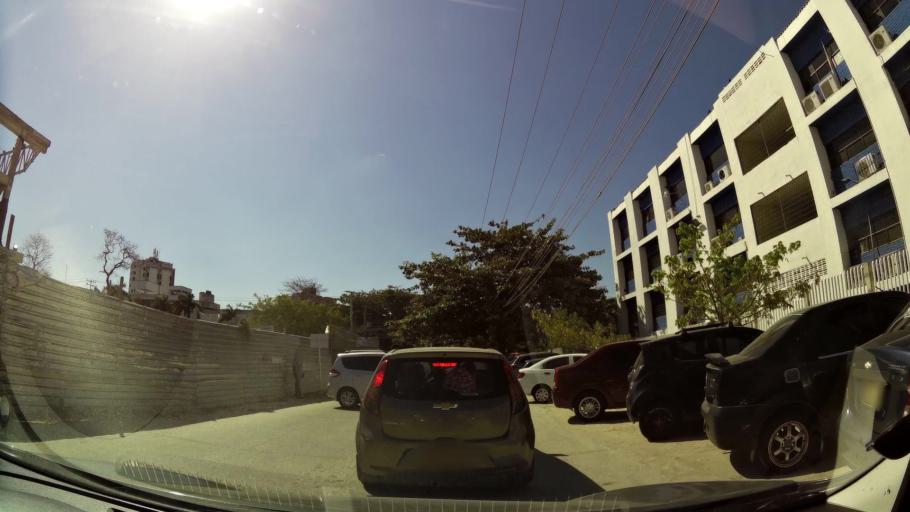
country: CO
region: Atlantico
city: Barranquilla
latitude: 10.9943
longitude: -74.7909
